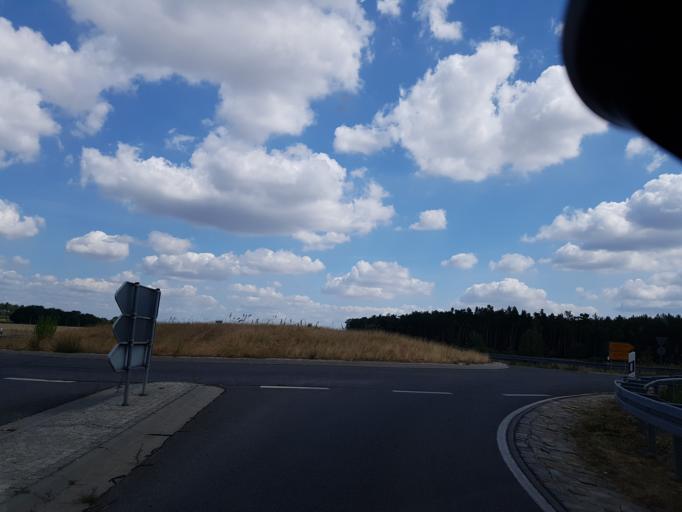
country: DE
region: Brandenburg
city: Drebkau
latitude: 51.6629
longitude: 14.2389
